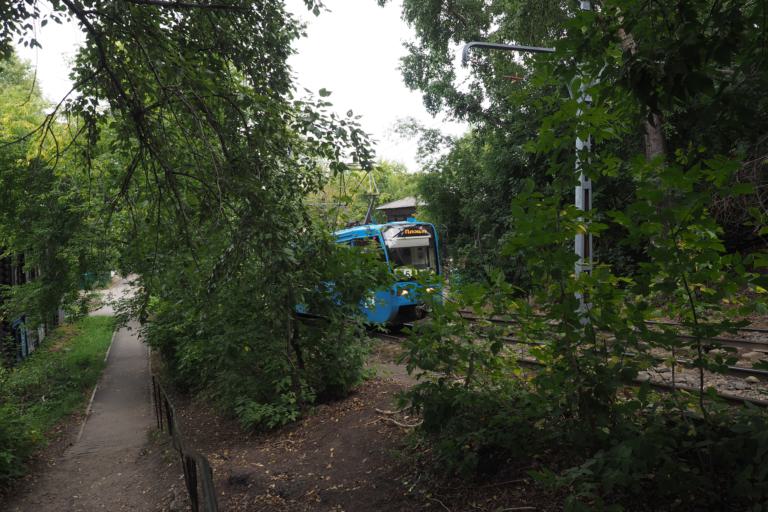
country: RU
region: Tomsk
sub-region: Tomskiy Rayon
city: Tomsk
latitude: 56.4811
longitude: 84.9530
